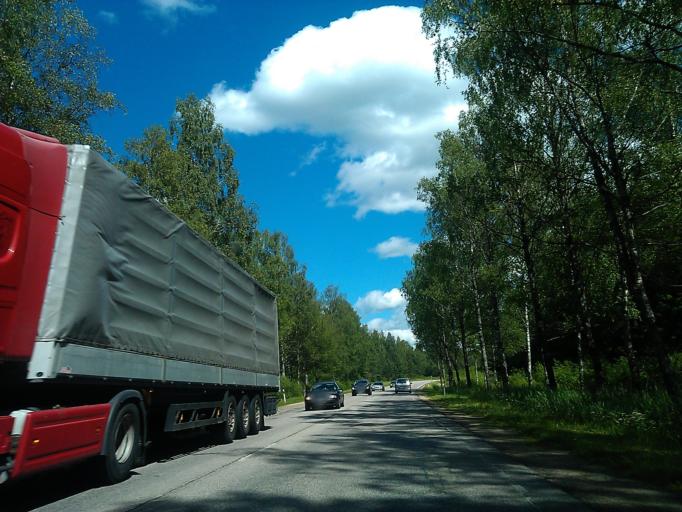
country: LV
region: Amatas Novads
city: Drabesi
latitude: 57.2198
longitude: 25.2100
